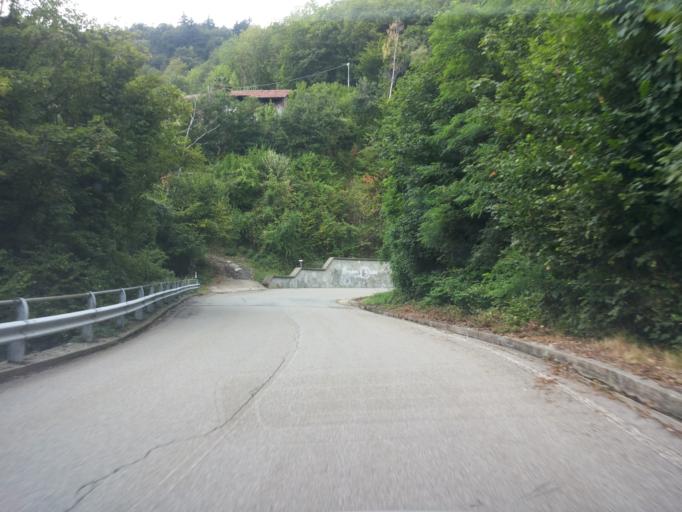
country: IT
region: Piedmont
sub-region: Provincia di Biella
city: Pollone
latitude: 45.5974
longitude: 7.9993
